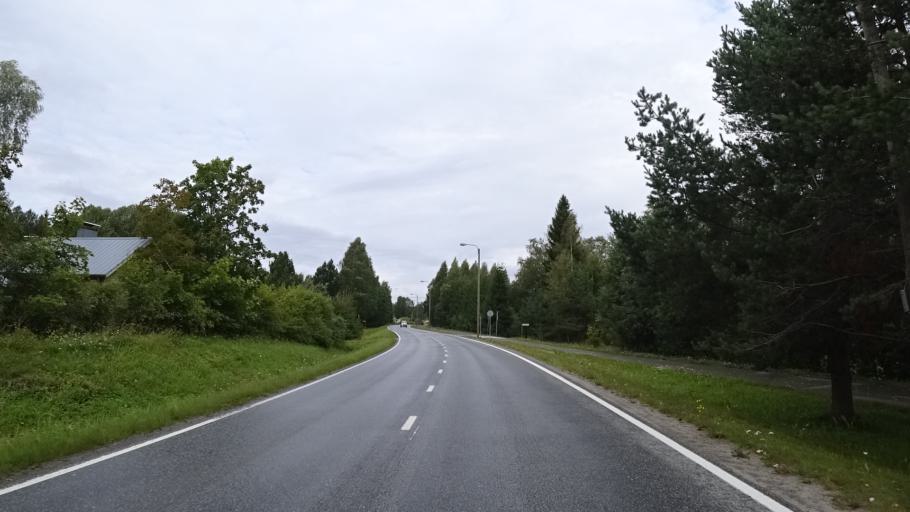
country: FI
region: Southern Savonia
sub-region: Savonlinna
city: Kerimaeki
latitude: 61.9220
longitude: 29.2811
